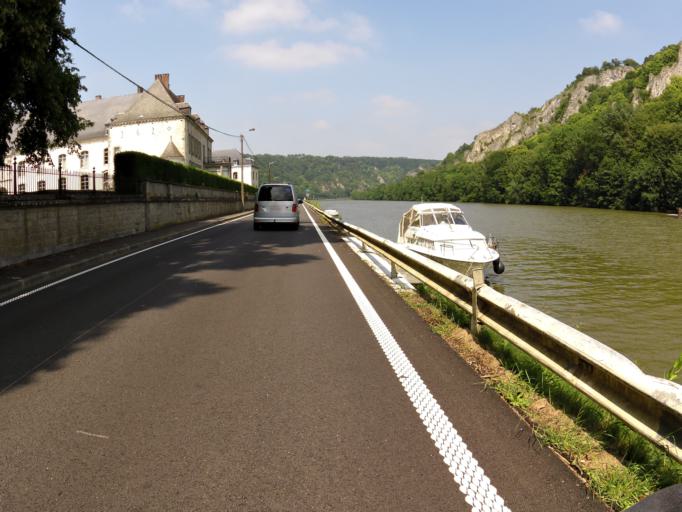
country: BE
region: Wallonia
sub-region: Province de Namur
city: Onhaye
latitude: 50.2058
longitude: 4.8675
